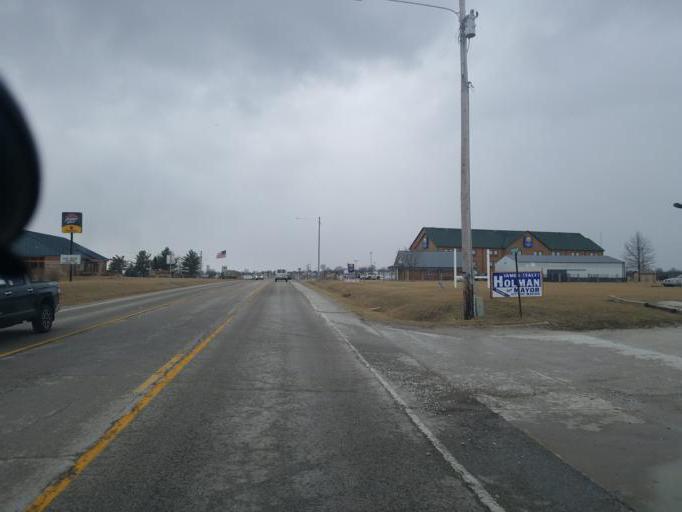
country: US
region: Missouri
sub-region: Macon County
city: Macon
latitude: 39.7593
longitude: -92.4676
